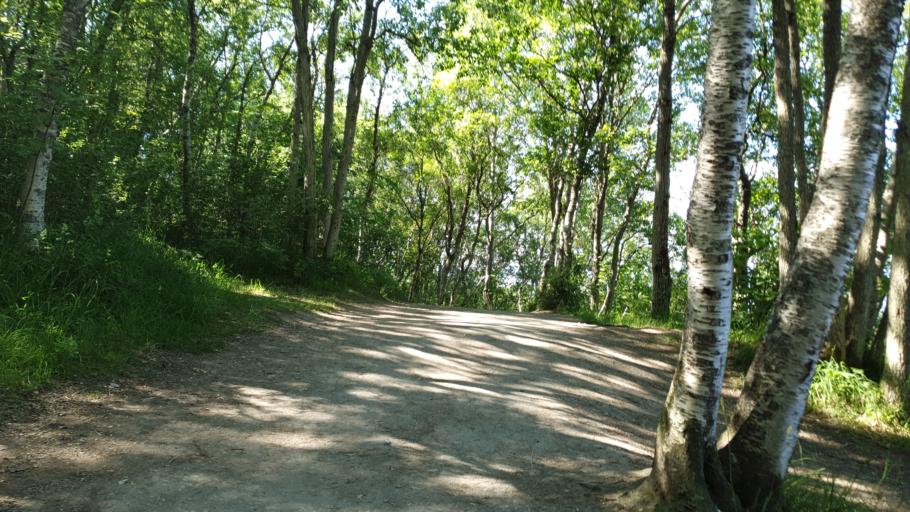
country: NO
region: Sor-Trondelag
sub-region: Trondheim
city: Trondheim
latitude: 63.4543
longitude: 10.4575
